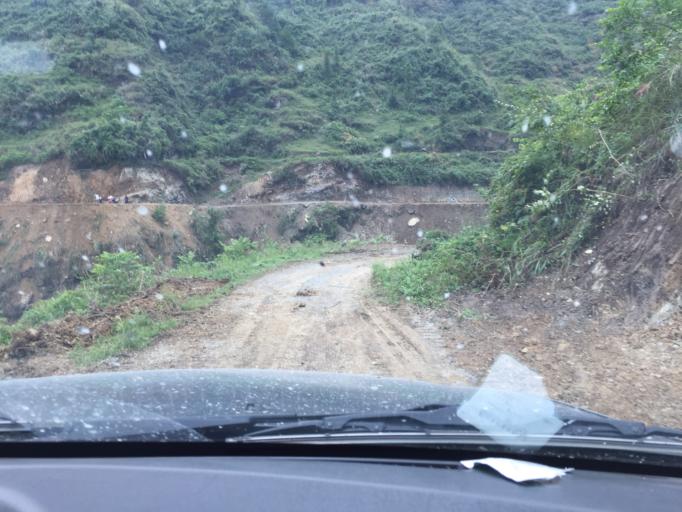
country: CN
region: Guizhou Sheng
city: Nangan
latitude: 28.2562
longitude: 107.9493
